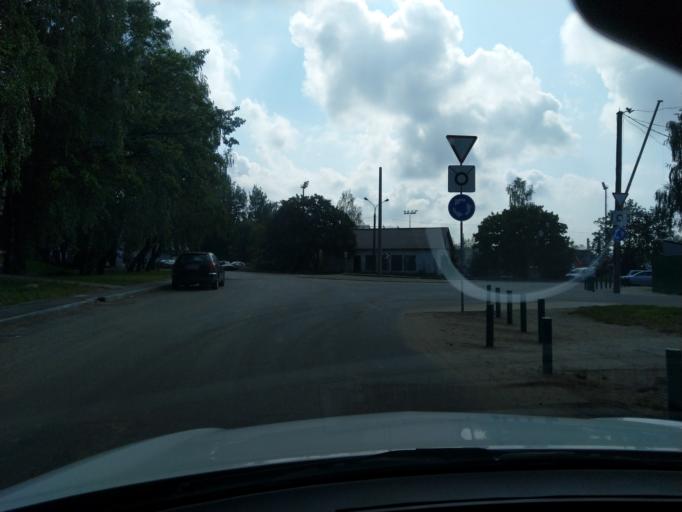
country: BY
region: Minsk
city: Zhdanovichy
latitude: 53.9063
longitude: 27.4133
